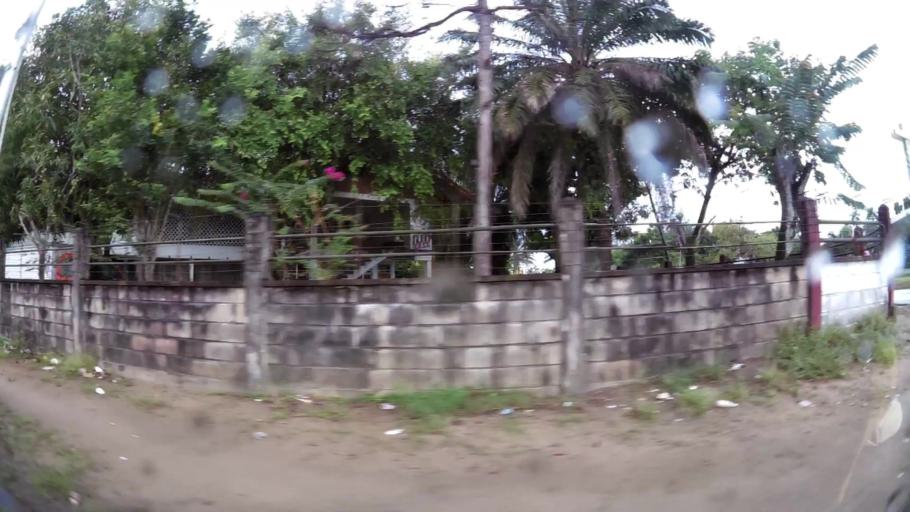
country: SR
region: Paramaribo
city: Paramaribo
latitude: 5.8145
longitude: -55.1793
